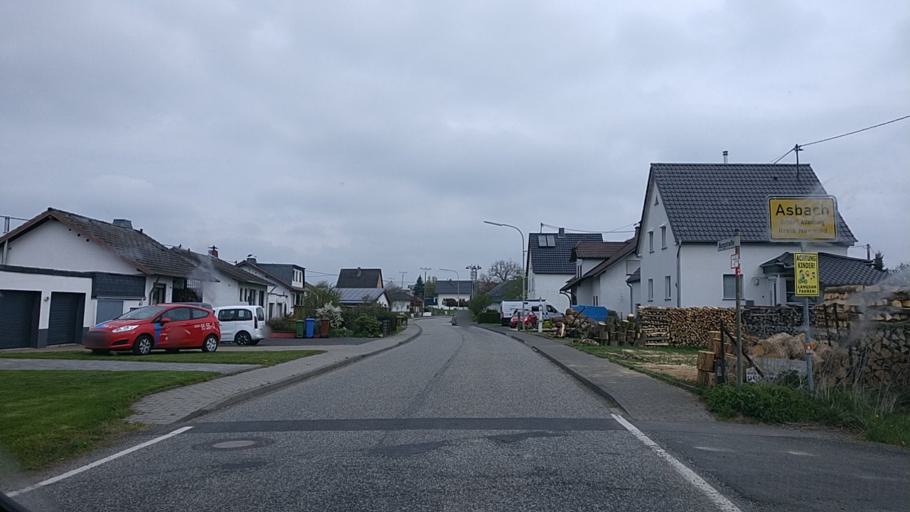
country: DE
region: Rheinland-Pfalz
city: Peterslahr
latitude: 50.6304
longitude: 7.4580
